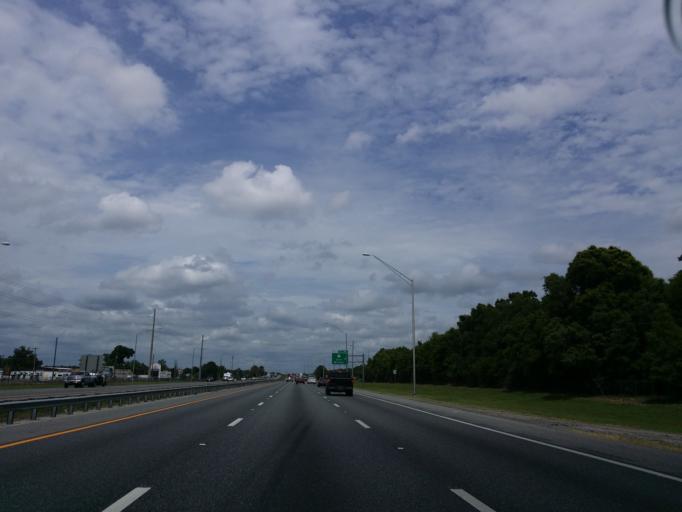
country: US
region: Florida
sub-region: Marion County
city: Ocala
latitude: 29.1994
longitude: -82.1845
